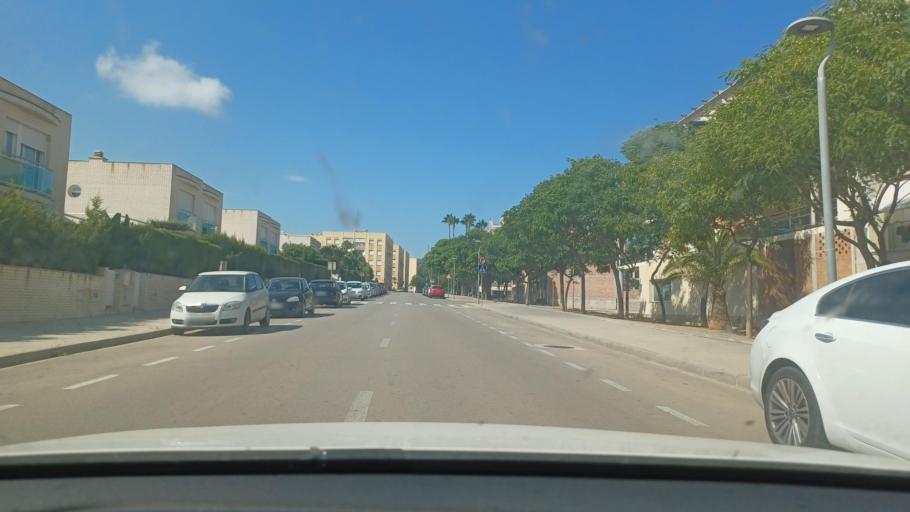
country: ES
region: Catalonia
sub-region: Provincia de Tarragona
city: Sant Carles de la Rapita
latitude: 40.6133
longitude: 0.5832
